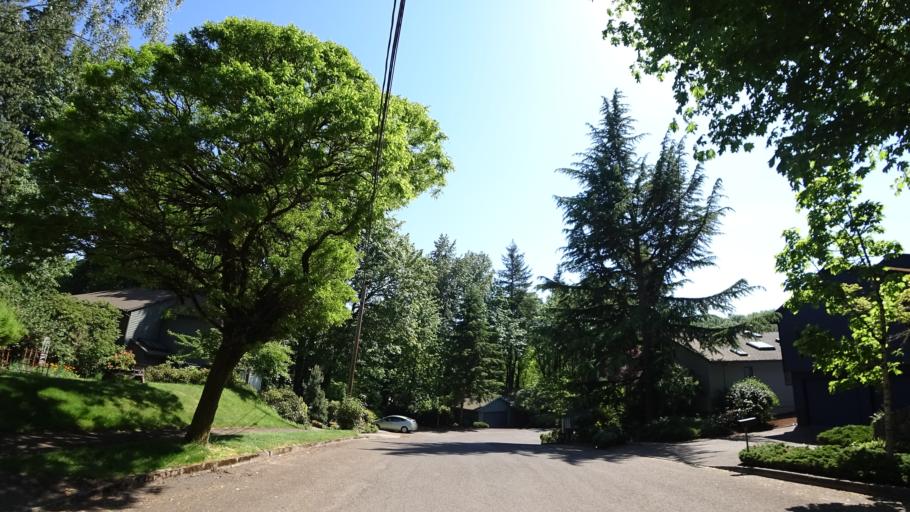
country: US
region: Oregon
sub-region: Clackamas County
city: Milwaukie
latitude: 45.4687
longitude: -122.6754
